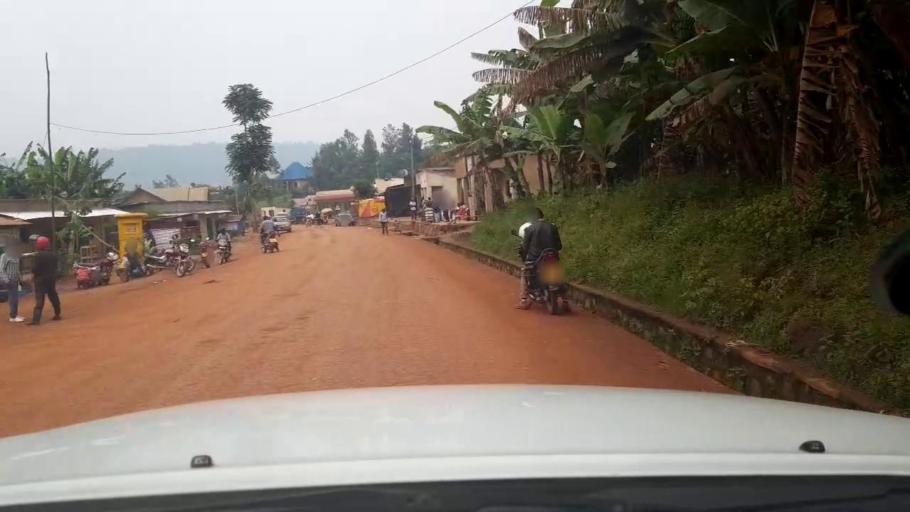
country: RW
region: Kigali
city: Kigali
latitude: -1.9021
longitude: 29.9696
